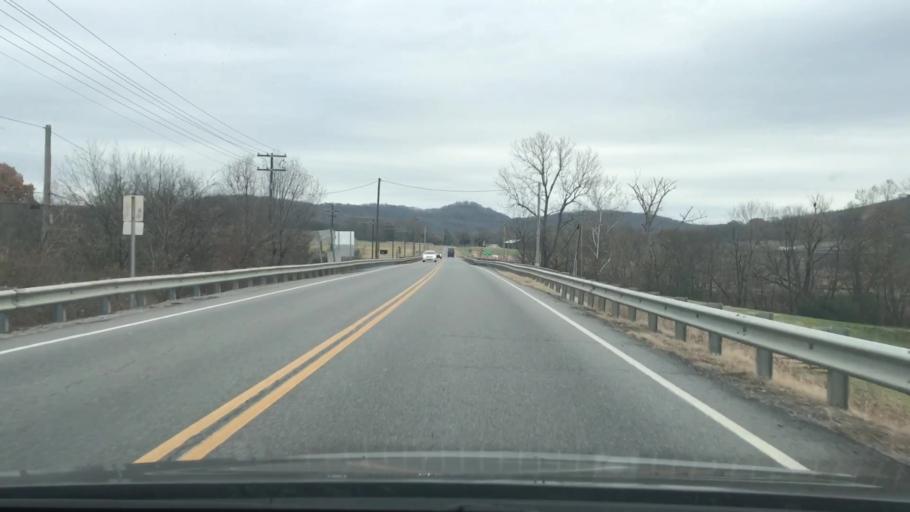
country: US
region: Tennessee
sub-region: Trousdale County
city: Hartsville
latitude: 36.3855
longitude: -86.1305
